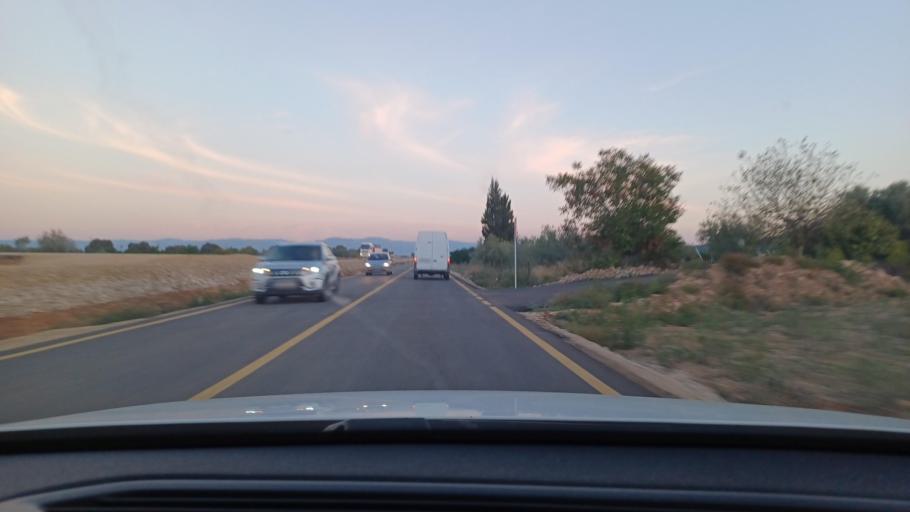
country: ES
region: Catalonia
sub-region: Provincia de Tarragona
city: Alcanar
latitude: 40.5337
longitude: 0.4432
